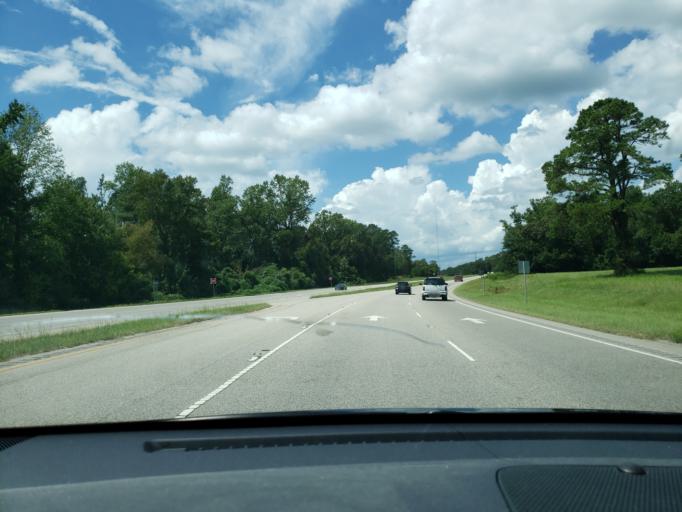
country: US
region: North Carolina
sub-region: Bladen County
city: Bladenboro
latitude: 34.7232
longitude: -78.7657
